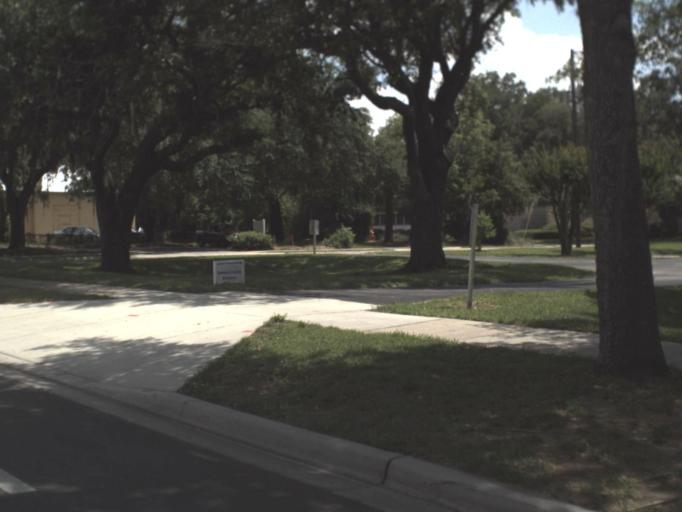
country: US
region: Florida
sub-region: Alachua County
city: Gainesville
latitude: 29.6564
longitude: -82.3250
